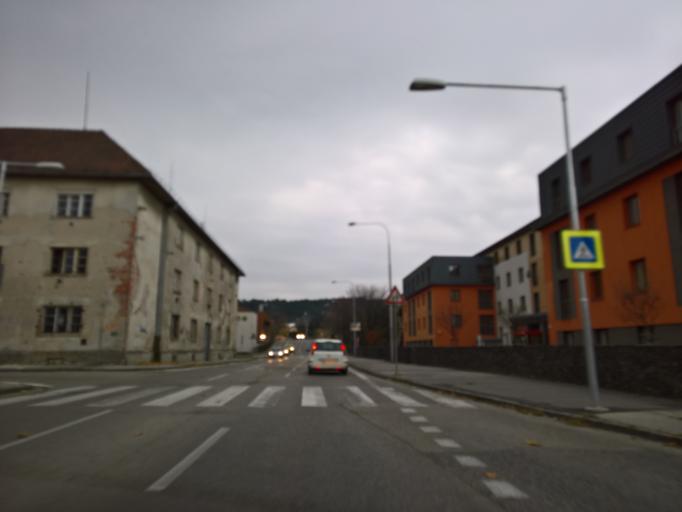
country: SK
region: Nitriansky
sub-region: Okres Nitra
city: Nitra
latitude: 48.3072
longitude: 18.0772
